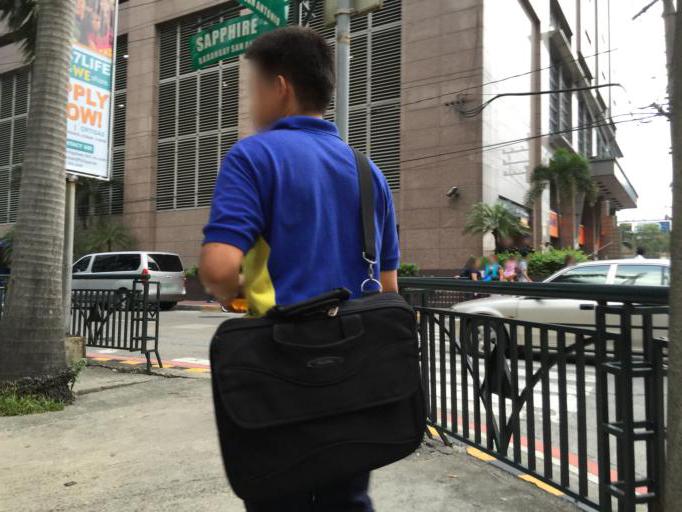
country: PH
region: Metro Manila
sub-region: Pasig
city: Pasig City
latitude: 14.5868
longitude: 121.0631
